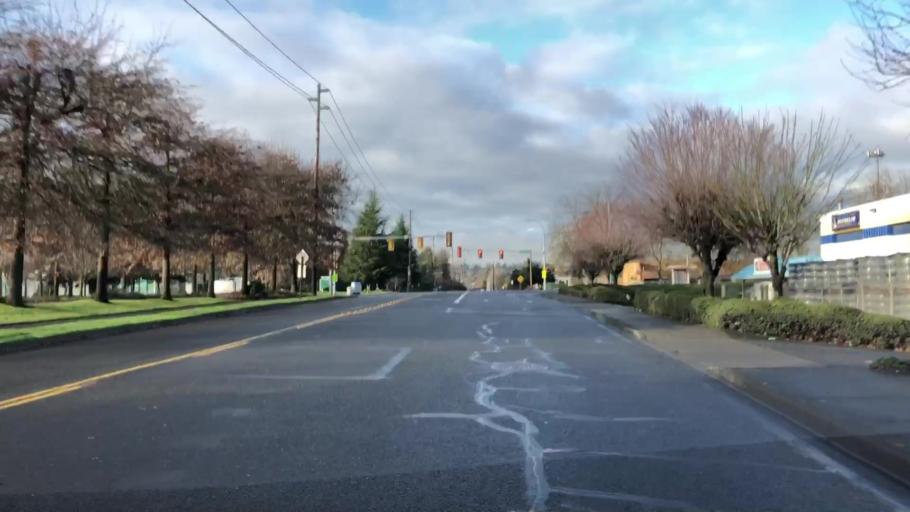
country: US
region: Washington
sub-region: King County
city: Renton
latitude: 47.4661
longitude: -122.2218
